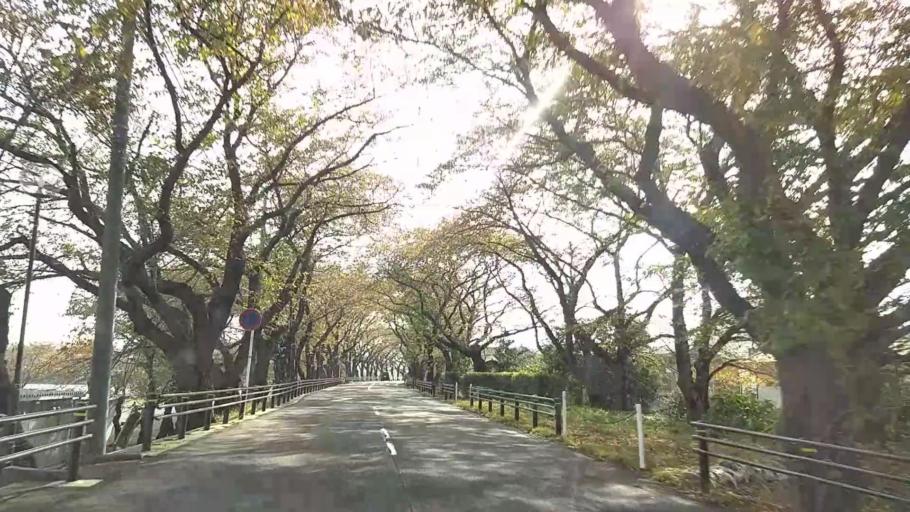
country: JP
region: Kanagawa
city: Atsugi
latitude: 35.4492
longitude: 139.3665
